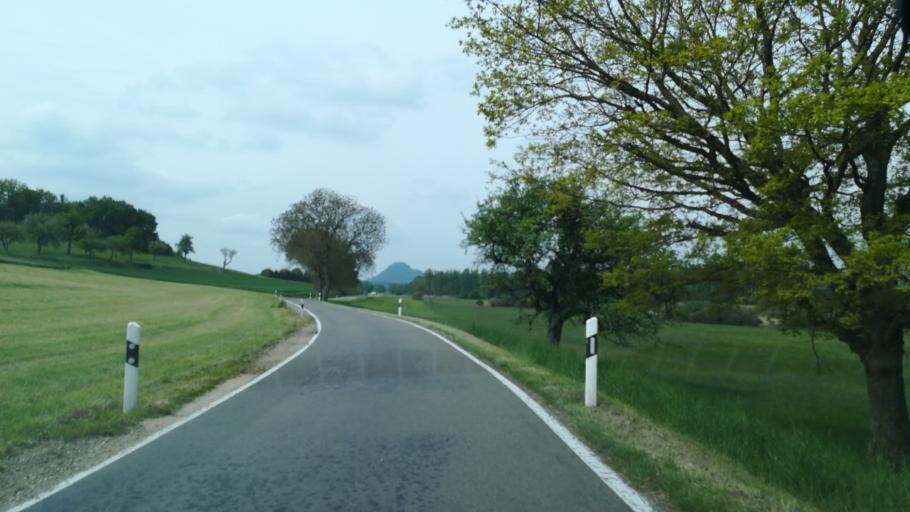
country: DE
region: Baden-Wuerttemberg
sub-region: Freiburg Region
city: Volkertshausen
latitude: 47.8038
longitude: 8.8915
